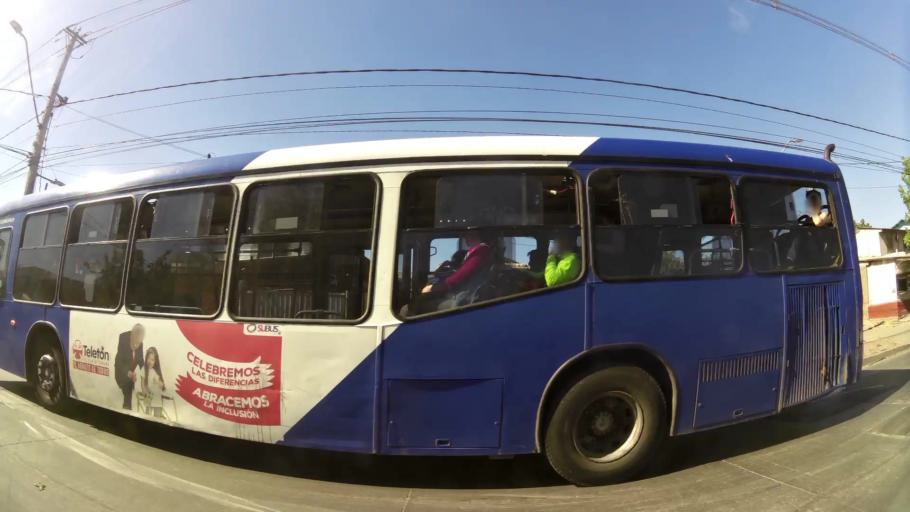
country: CL
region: Santiago Metropolitan
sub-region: Provincia de Maipo
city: San Bernardo
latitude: -33.5895
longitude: -70.6708
